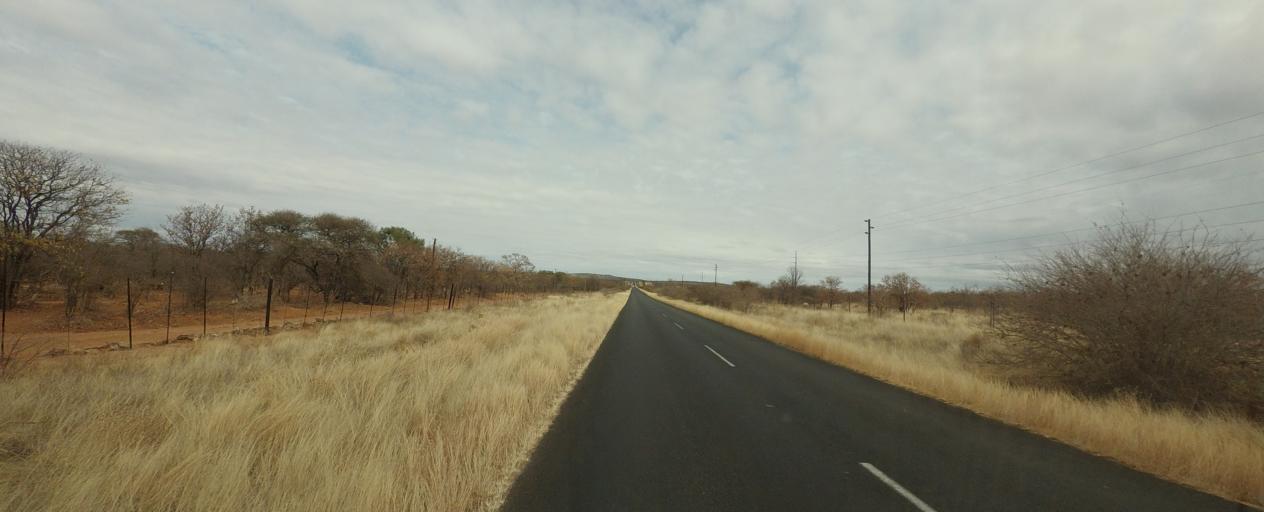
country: ZW
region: Matabeleland South
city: Beitbridge
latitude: -22.4302
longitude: 29.4411
